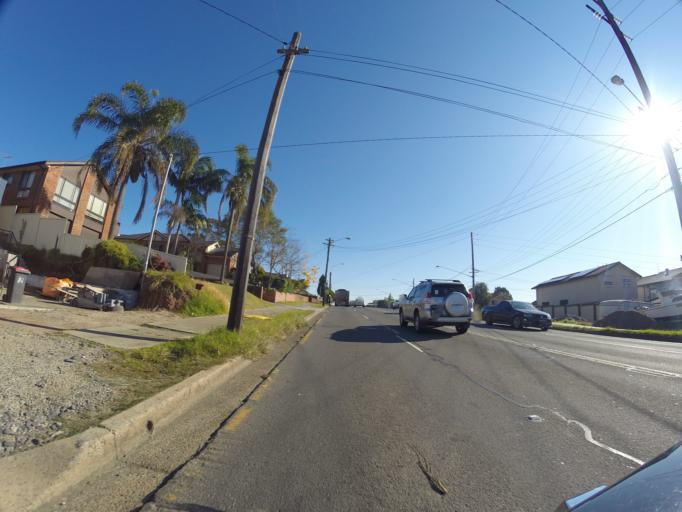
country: AU
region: New South Wales
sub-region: Hurstville
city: Penshurst
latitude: -33.9559
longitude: 151.0862
